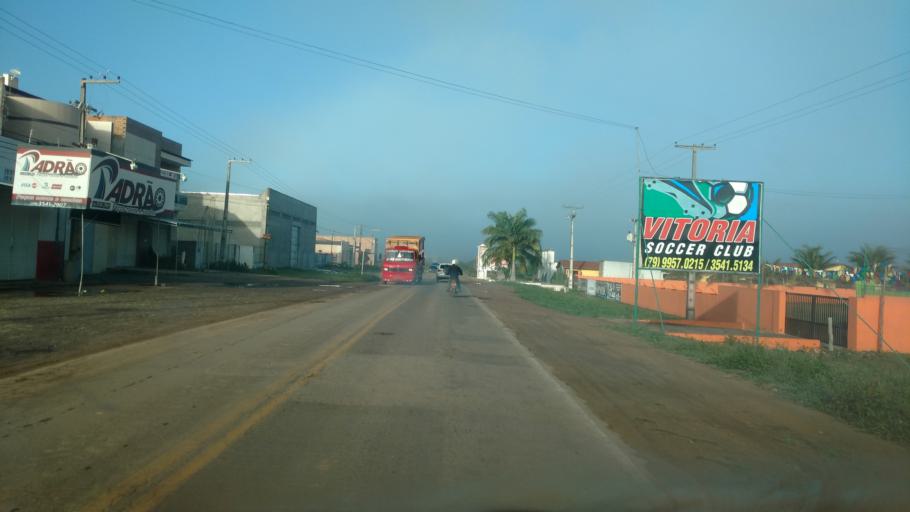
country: BR
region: Sergipe
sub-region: Tobias Barreto
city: Tobias Barreto
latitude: -11.1733
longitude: -37.9884
